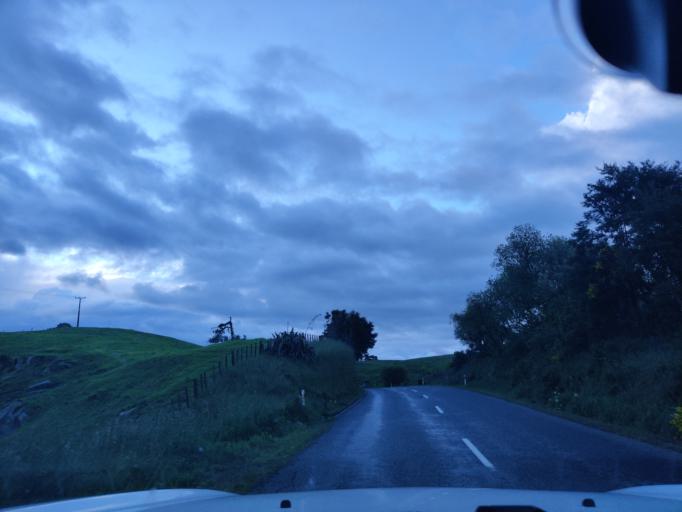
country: NZ
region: Waikato
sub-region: South Waikato District
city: Tokoroa
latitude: -38.1921
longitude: 175.7999
